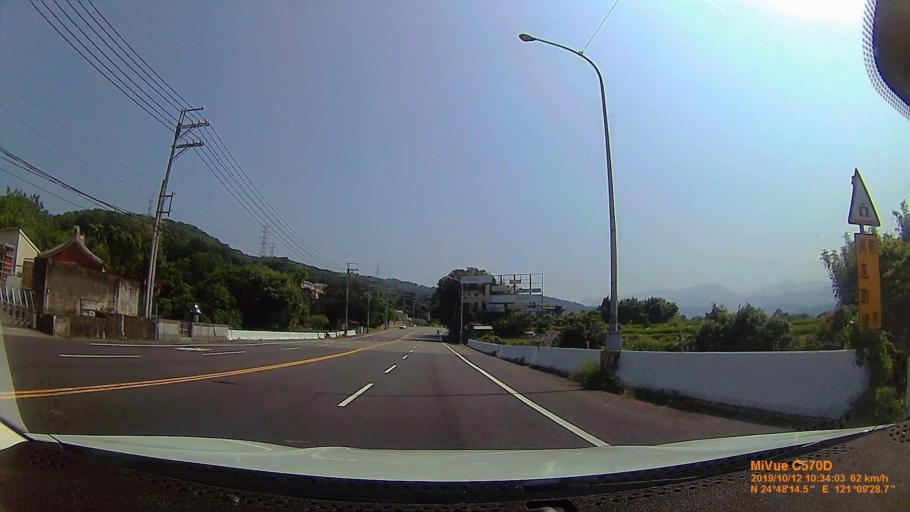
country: TW
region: Taiwan
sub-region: Hsinchu
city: Zhubei
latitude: 24.8041
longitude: 121.1581
